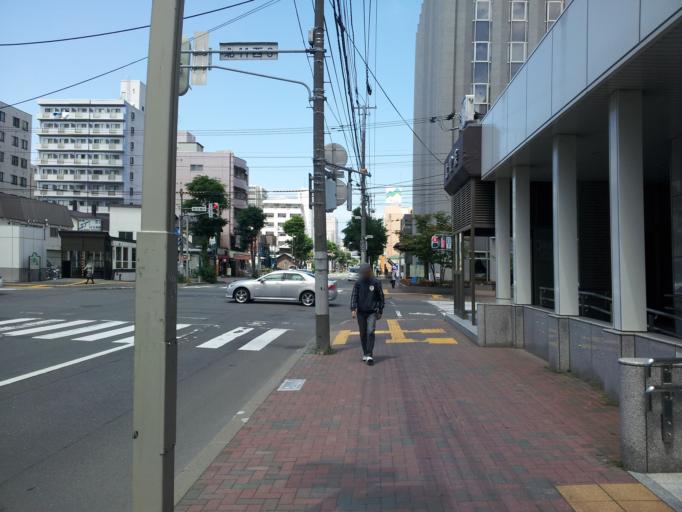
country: JP
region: Hokkaido
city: Sapporo
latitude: 43.0745
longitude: 141.3488
